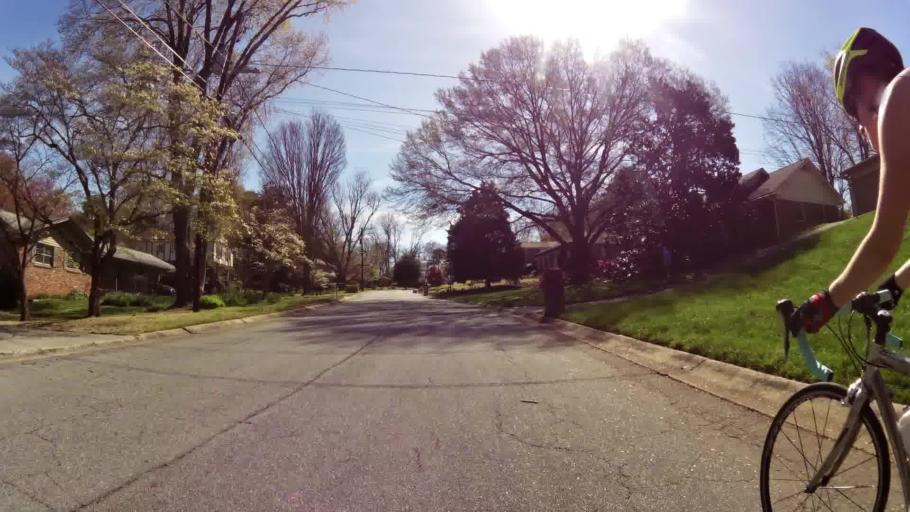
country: US
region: Georgia
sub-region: DeKalb County
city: Clarkston
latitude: 33.8234
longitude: -84.2701
